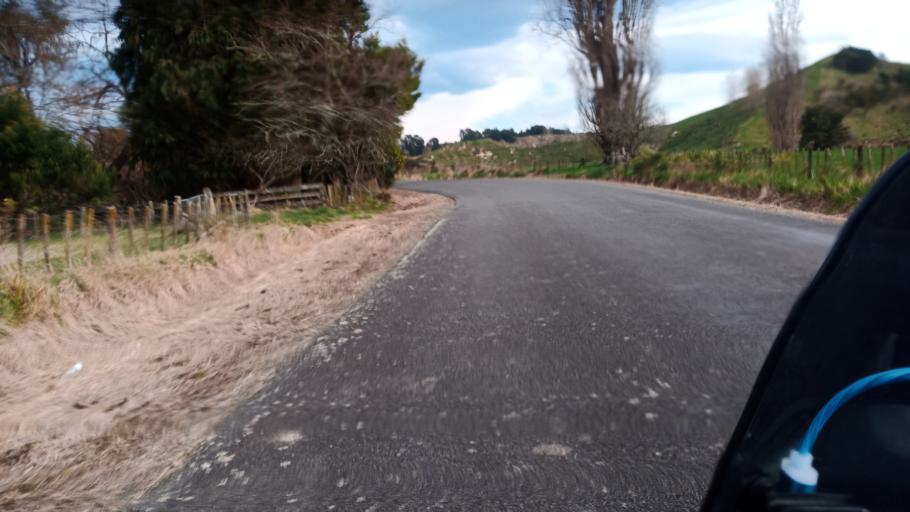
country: NZ
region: Hawke's Bay
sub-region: Wairoa District
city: Wairoa
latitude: -38.9661
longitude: 177.4383
